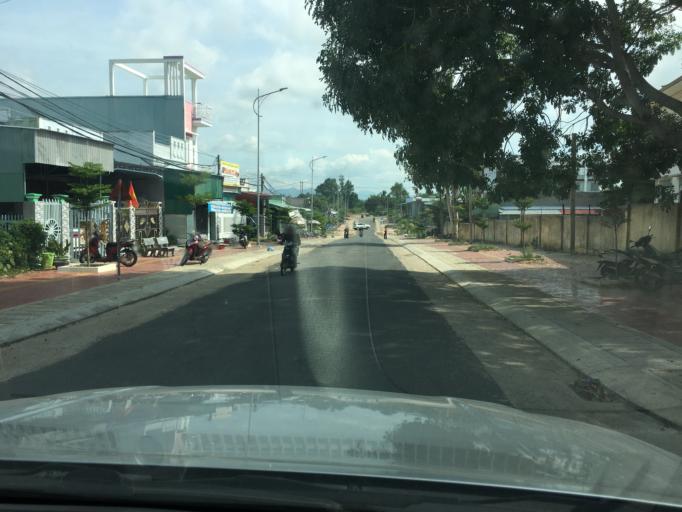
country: VN
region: Gia Lai
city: Kong Chro
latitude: 13.7750
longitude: 108.5221
